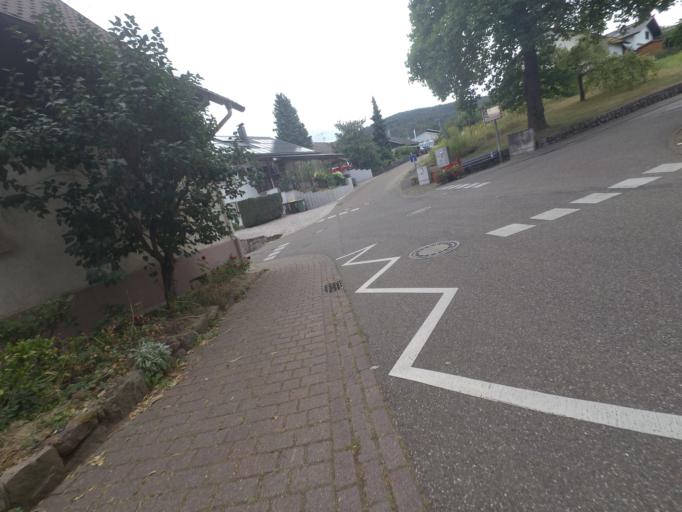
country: DE
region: Baden-Wuerttemberg
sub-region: Karlsruhe Region
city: Sinzheim
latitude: 48.7666
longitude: 8.1832
